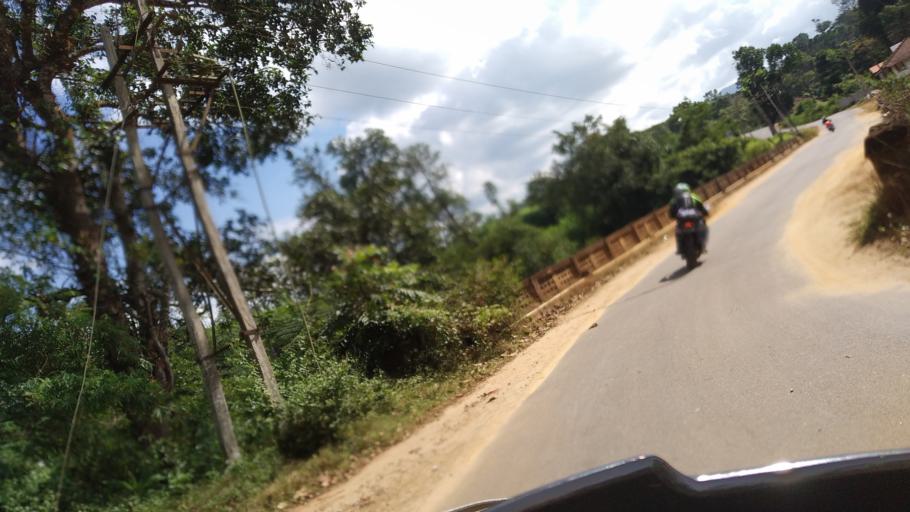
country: IN
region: Karnataka
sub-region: Kodagu
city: Ponnampet
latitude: 12.0329
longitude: 75.9348
